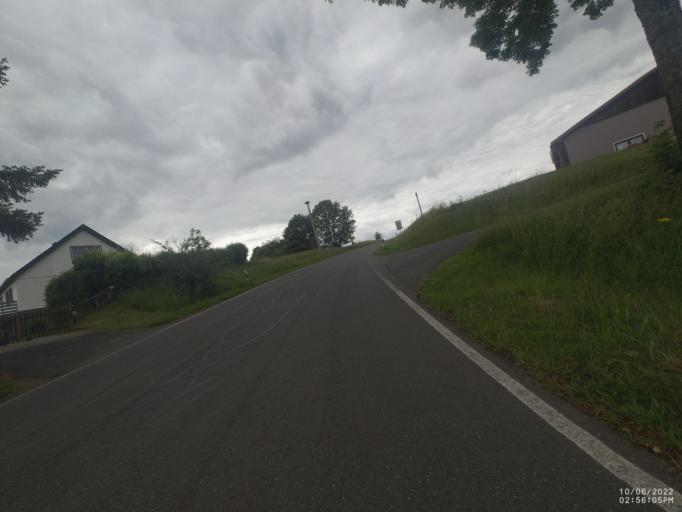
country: DE
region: Rheinland-Pfalz
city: Kopp
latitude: 50.1754
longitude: 6.5821
